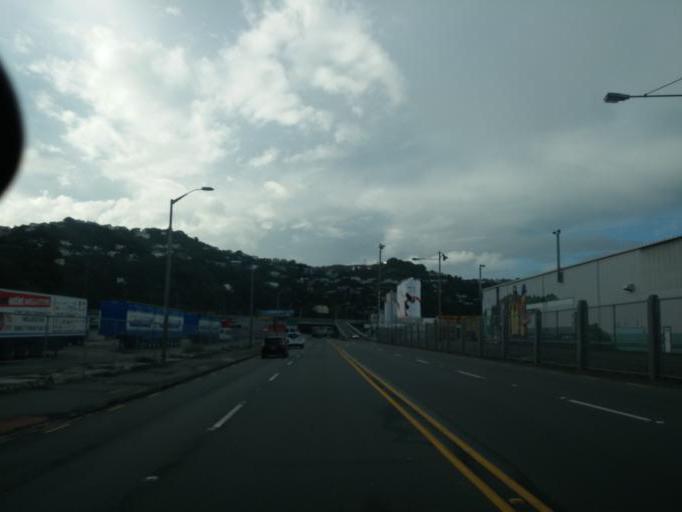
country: NZ
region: Wellington
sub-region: Wellington City
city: Wellington
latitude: -41.2691
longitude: 174.7861
